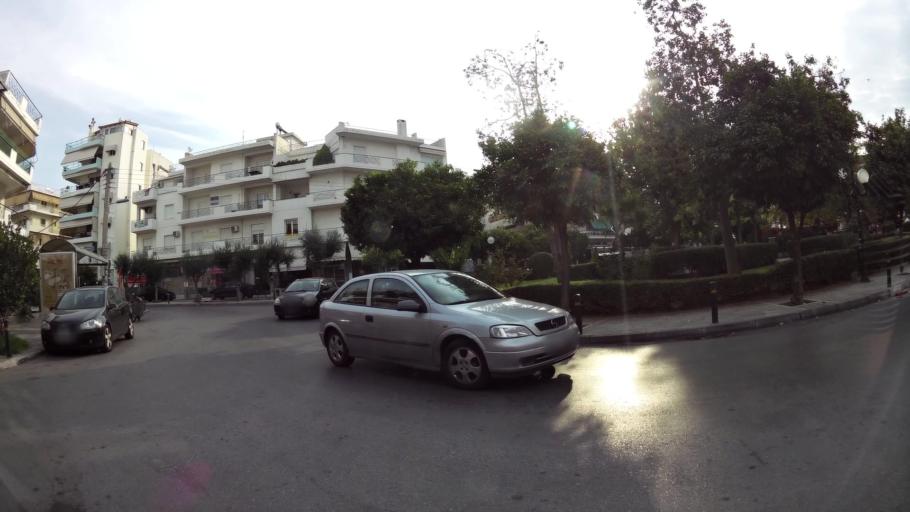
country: GR
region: Attica
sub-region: Nomarchia Athinas
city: Palaio Faliro
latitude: 37.9316
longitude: 23.7031
